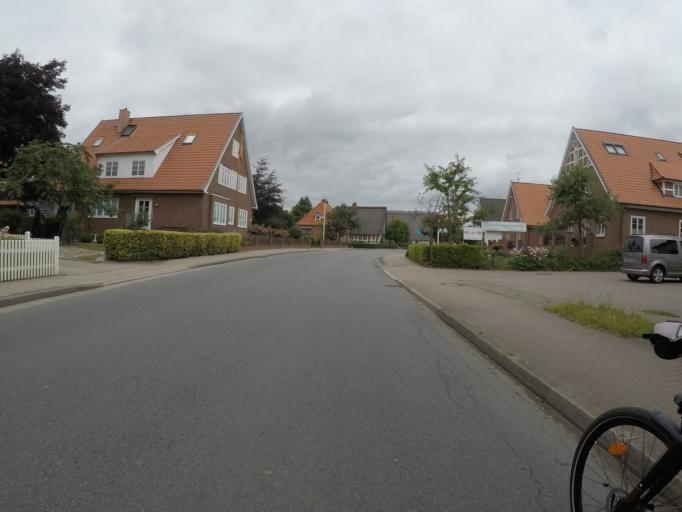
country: DE
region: Lower Saxony
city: Steinkirchen
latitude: 53.5641
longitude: 9.6099
